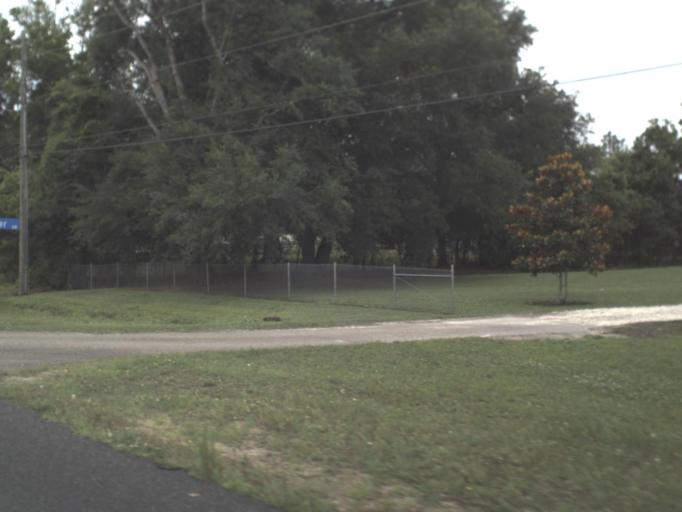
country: US
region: Florida
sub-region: Nassau County
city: Yulee
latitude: 30.6154
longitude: -81.7188
